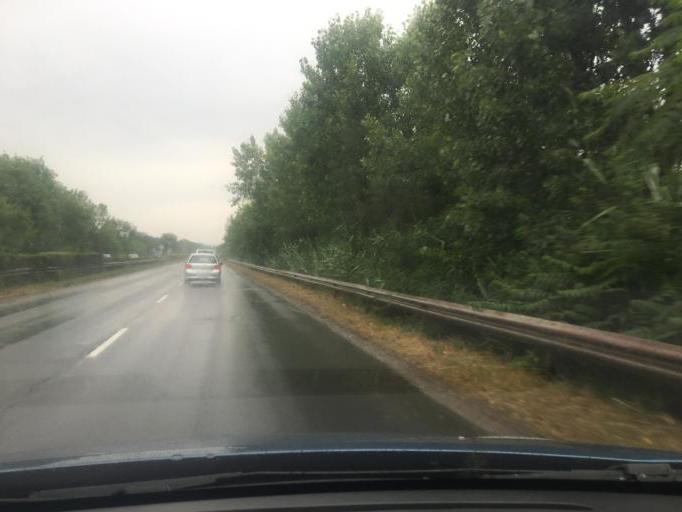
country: BG
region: Burgas
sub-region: Obshtina Burgas
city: Burgas
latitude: 42.5362
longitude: 27.4714
